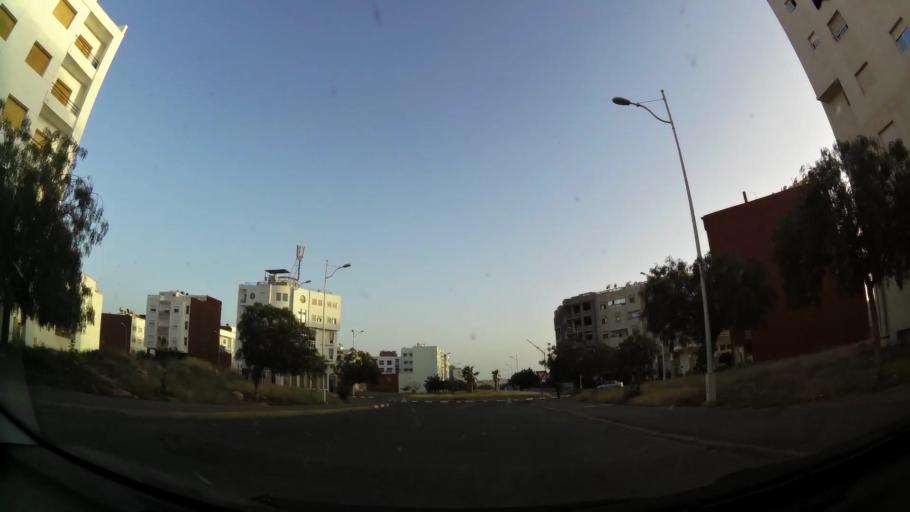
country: MA
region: Oued ed Dahab-Lagouira
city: Dakhla
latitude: 30.3939
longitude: -9.5657
